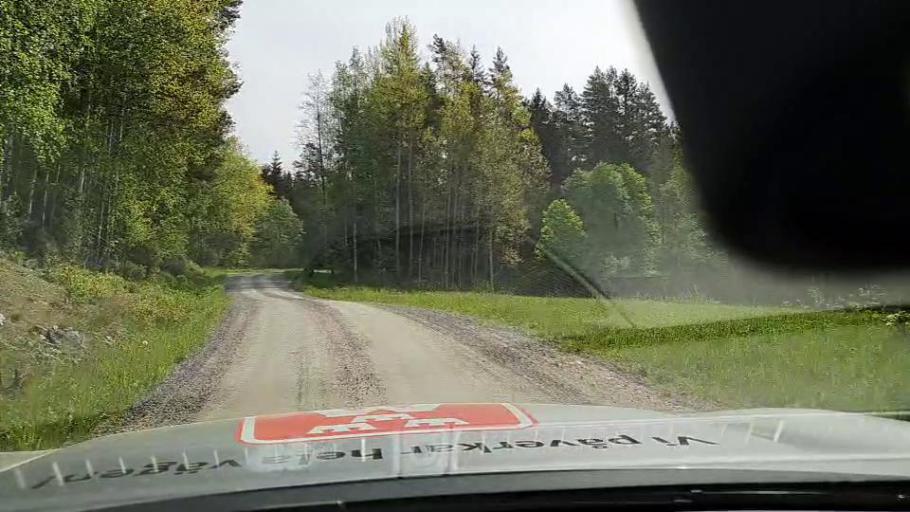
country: SE
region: Soedermanland
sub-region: Flens Kommun
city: Malmkoping
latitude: 59.2615
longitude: 16.8671
